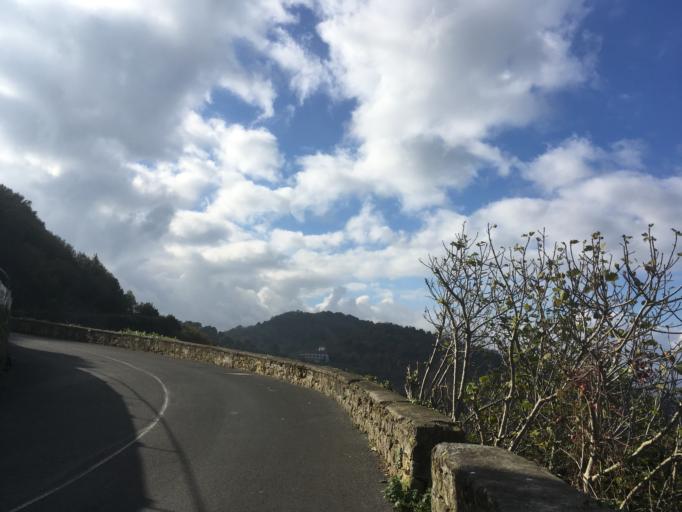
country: ES
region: Basque Country
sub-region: Provincia de Guipuzcoa
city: San Sebastian
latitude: 43.3228
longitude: -2.0104
